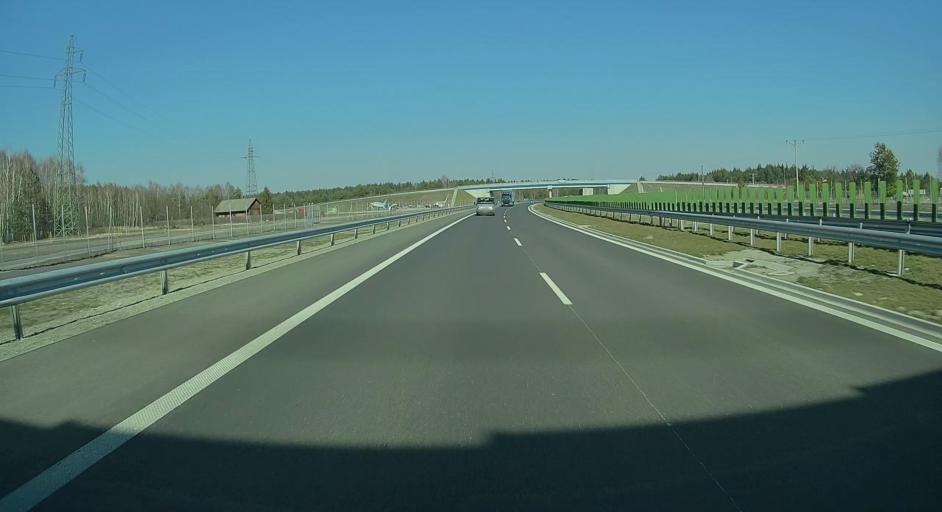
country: PL
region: Subcarpathian Voivodeship
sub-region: Powiat nizanski
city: Konczyce
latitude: 50.4220
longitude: 22.1285
